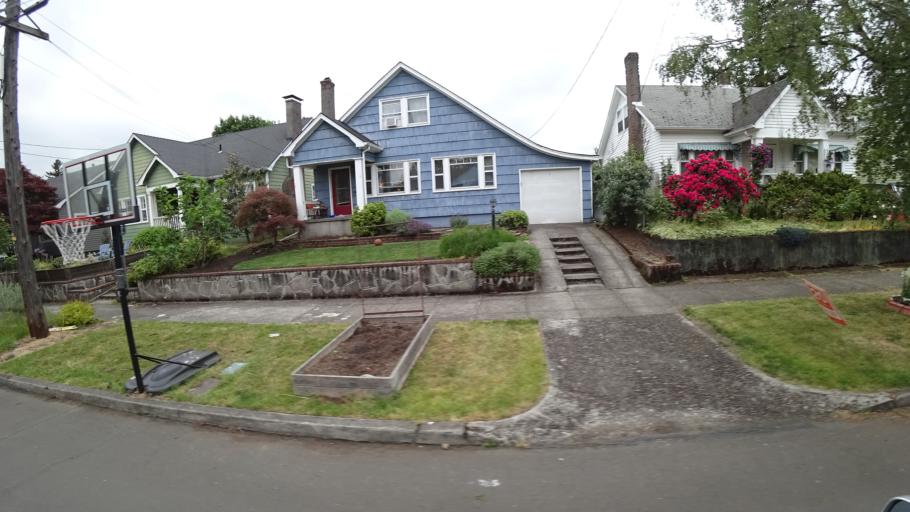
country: US
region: Oregon
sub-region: Multnomah County
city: Portland
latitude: 45.5475
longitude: -122.6077
